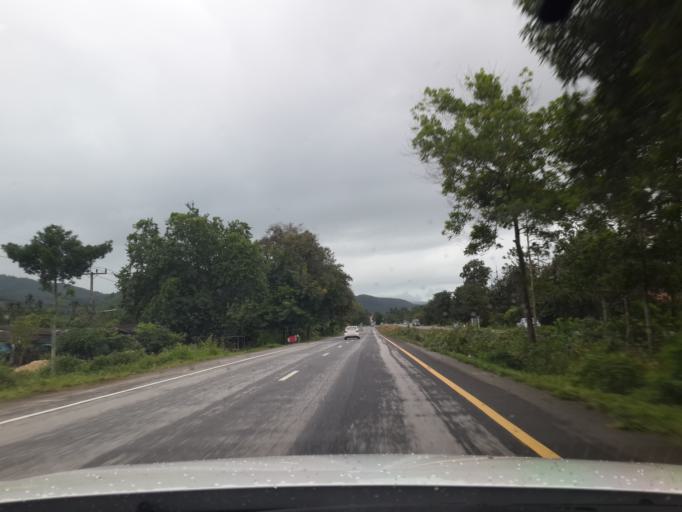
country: TH
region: Songkhla
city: Na Mom
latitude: 6.9660
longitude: 100.5122
